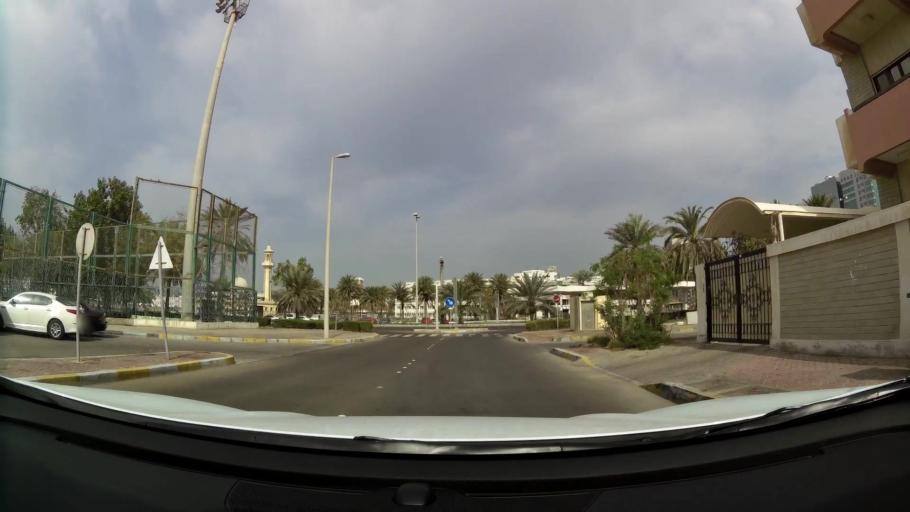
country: AE
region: Abu Dhabi
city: Abu Dhabi
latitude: 24.4611
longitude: 54.3758
